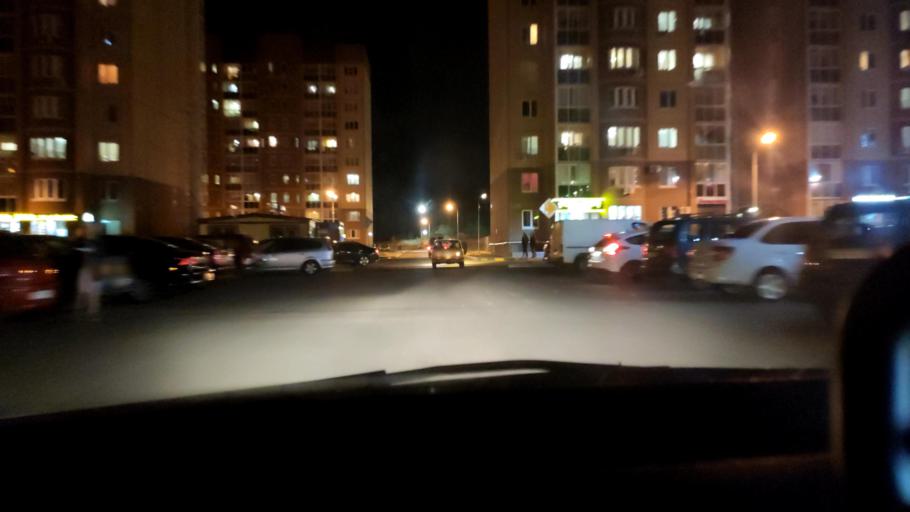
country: RU
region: Voronezj
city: Shilovo
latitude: 51.5713
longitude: 39.1250
